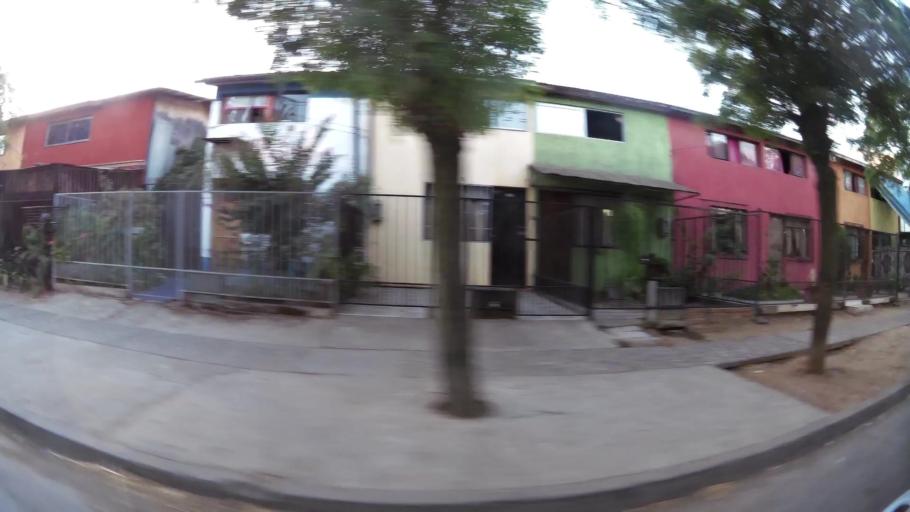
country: CL
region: Maule
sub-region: Provincia de Talca
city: Talca
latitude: -35.4461
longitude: -71.6314
